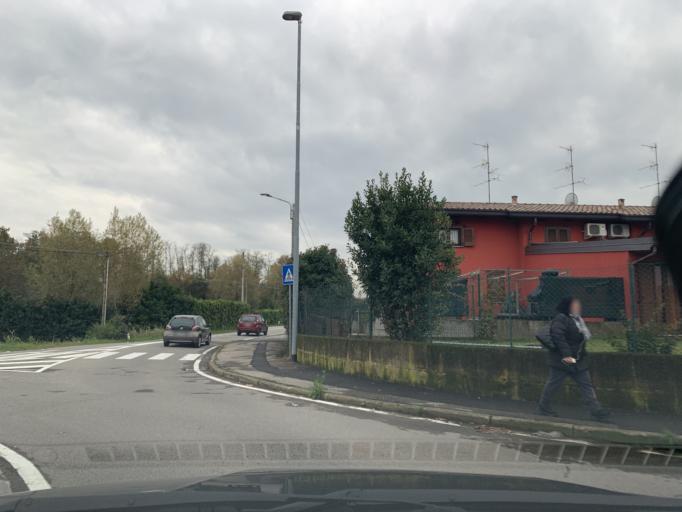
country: IT
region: Lombardy
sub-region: Provincia di Como
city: Bulgorello
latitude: 45.7224
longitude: 9.0537
